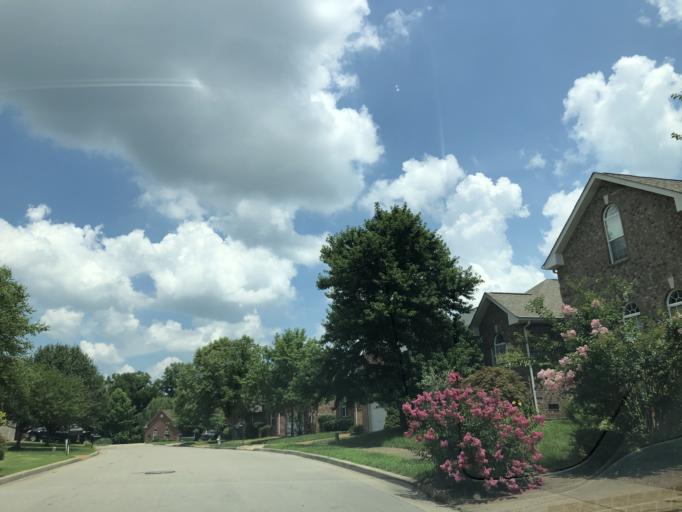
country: US
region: Tennessee
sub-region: Williamson County
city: Brentwood Estates
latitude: 36.0182
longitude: -86.7131
